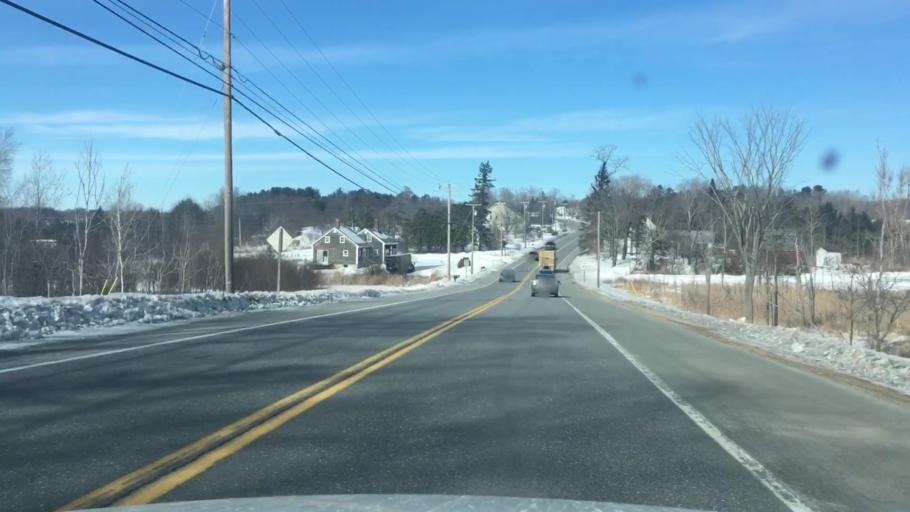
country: US
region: Maine
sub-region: Penobscot County
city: Orrington
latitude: 44.7164
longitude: -68.8272
